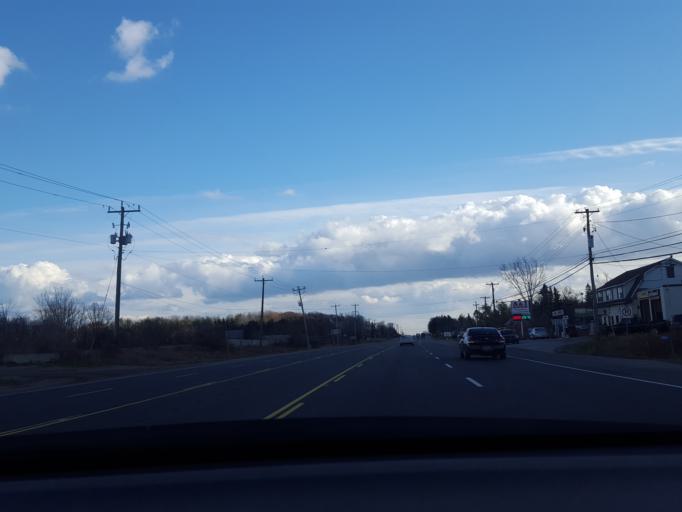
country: CA
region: Ontario
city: Ancaster
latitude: 43.3372
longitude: -79.9521
